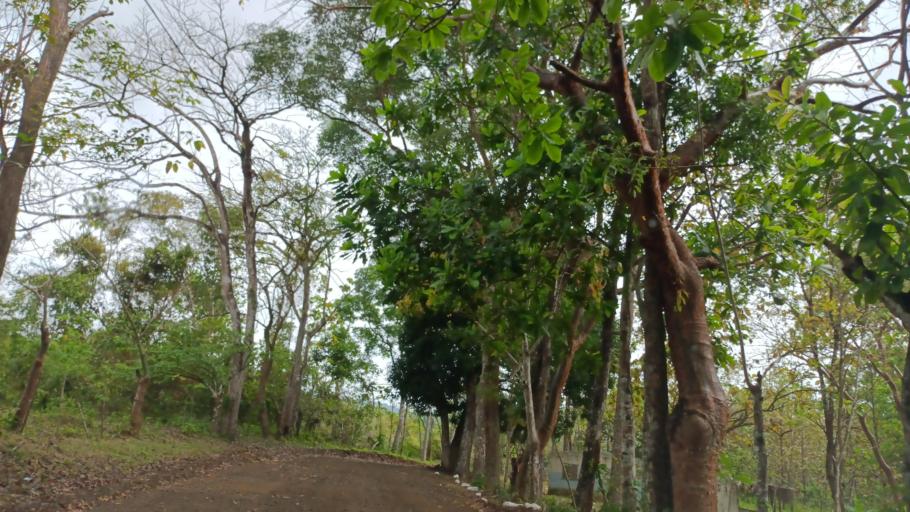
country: PA
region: Panama
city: La Cabima
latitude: 9.1322
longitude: -79.5156
